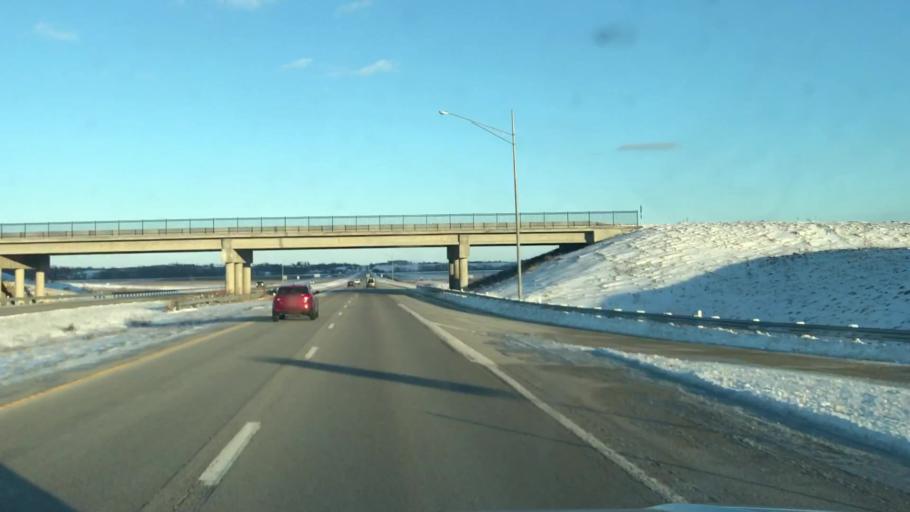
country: US
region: Missouri
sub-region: Buchanan County
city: Saint Joseph
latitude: 39.7479
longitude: -94.7510
